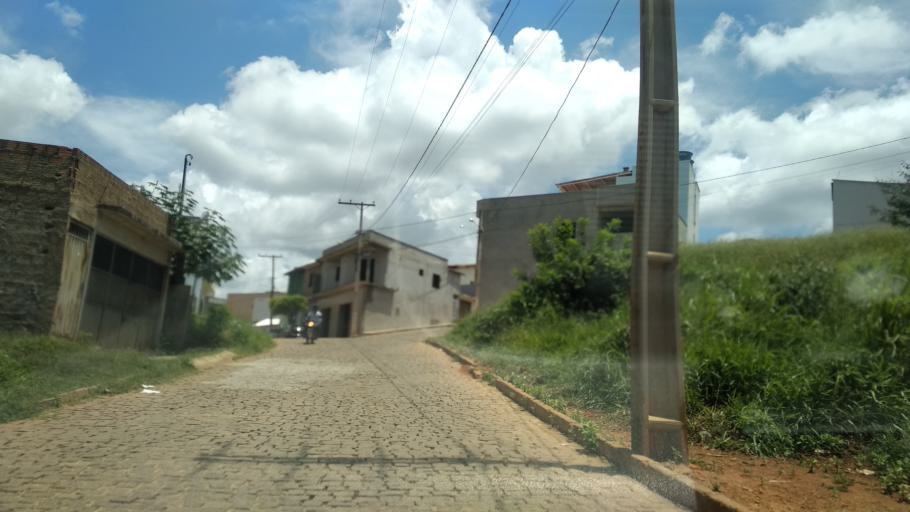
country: BR
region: Bahia
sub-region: Caetite
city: Caetite
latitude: -14.0616
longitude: -42.4888
